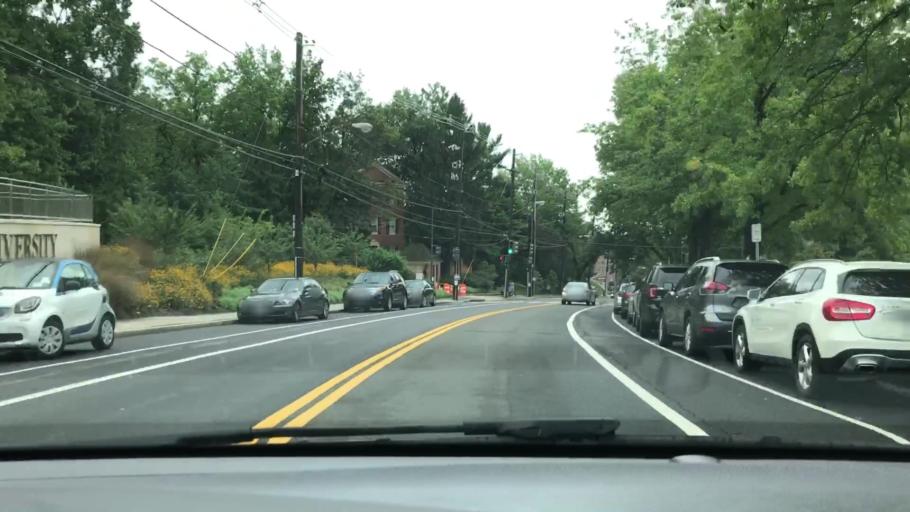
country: US
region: Maryland
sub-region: Montgomery County
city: Friendship Village
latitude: 38.9352
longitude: -77.0869
